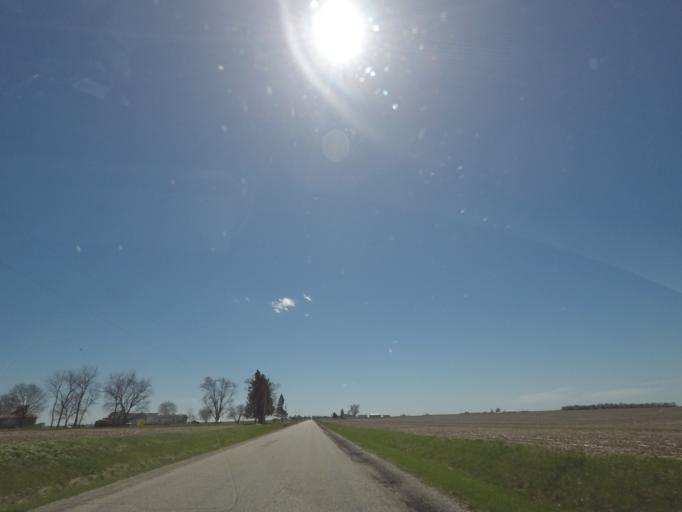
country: US
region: Illinois
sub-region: Logan County
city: Atlanta
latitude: 40.1714
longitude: -89.1937
